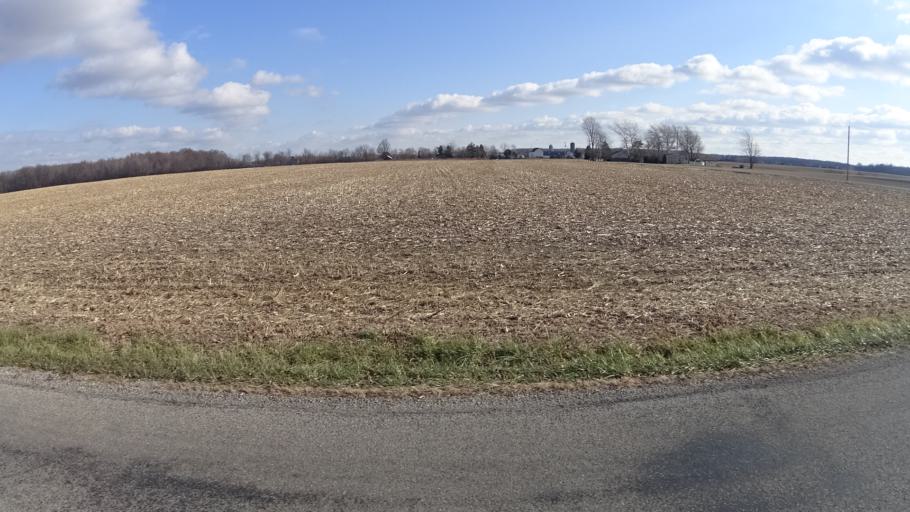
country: US
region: Ohio
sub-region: Lorain County
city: Camden
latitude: 41.2381
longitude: -82.2893
